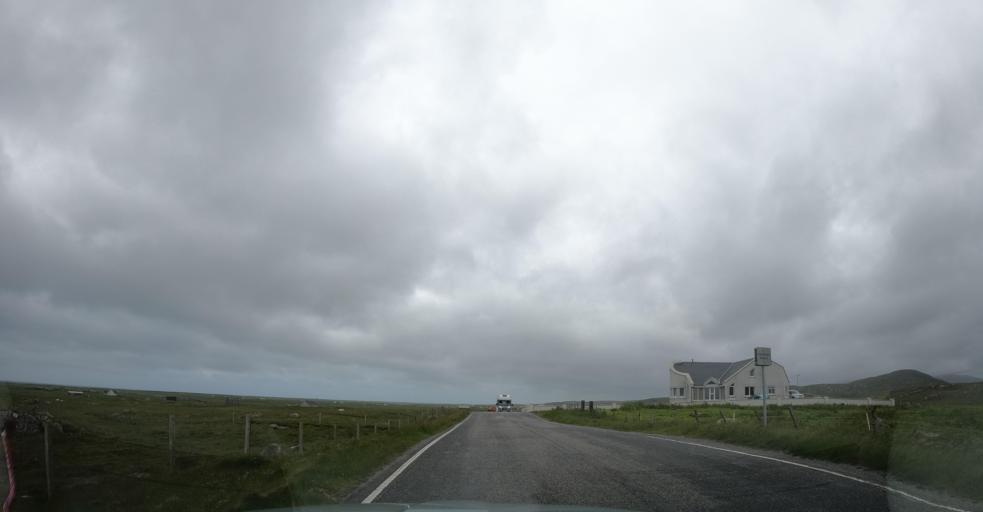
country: GB
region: Scotland
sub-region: Eilean Siar
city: Isle of South Uist
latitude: 57.1997
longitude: -7.3909
